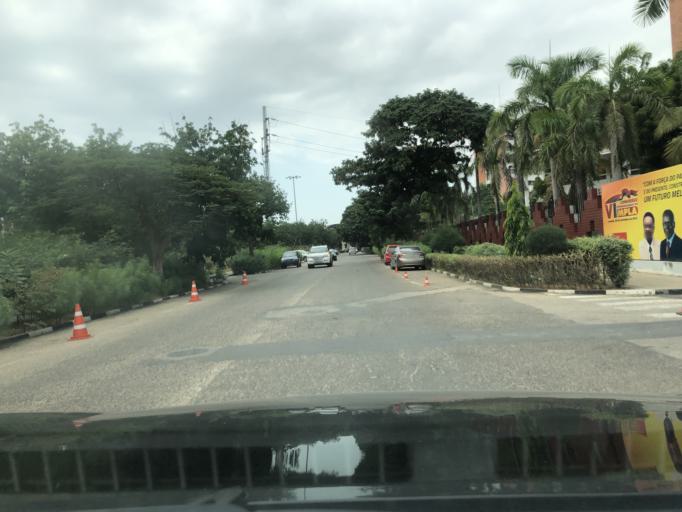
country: AO
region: Luanda
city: Luanda
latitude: -8.8297
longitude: 13.2402
